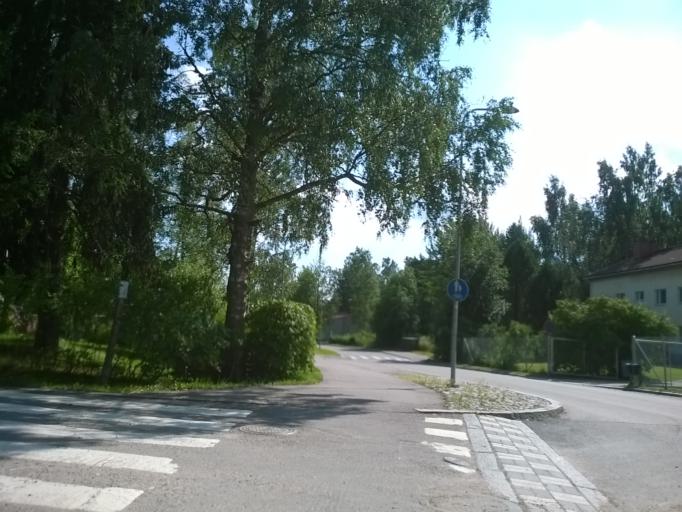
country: FI
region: Uusimaa
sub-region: Helsinki
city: Teekkarikylae
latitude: 60.2516
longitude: 24.8886
